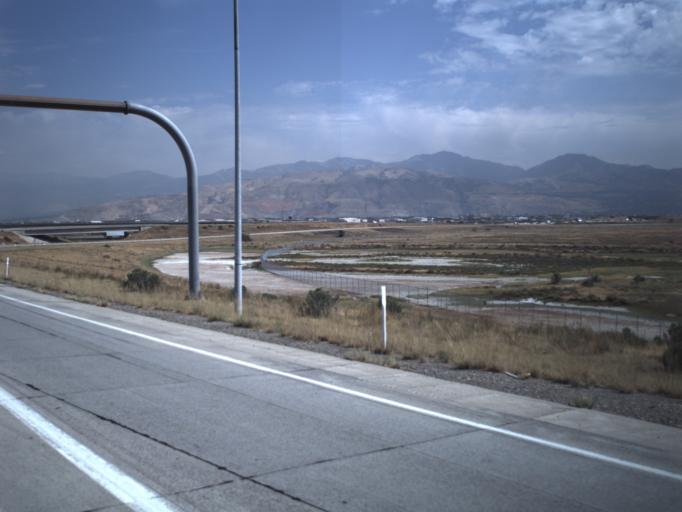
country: US
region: Utah
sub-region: Salt Lake County
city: West Valley City
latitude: 40.7601
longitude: -111.9862
